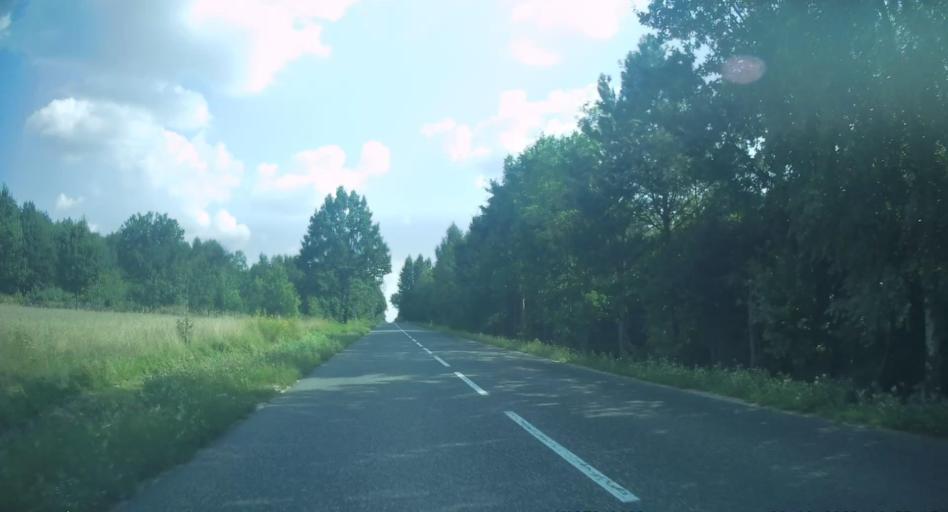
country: PL
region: Swietokrzyskie
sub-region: Powiat kielecki
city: Lopuszno
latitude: 50.9291
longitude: 20.2385
